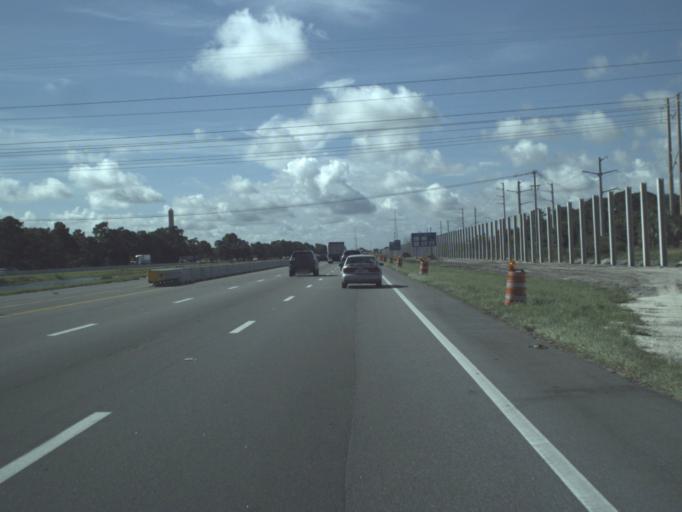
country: US
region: Florida
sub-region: Sarasota County
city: The Meadows
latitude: 27.3580
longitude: -82.4468
